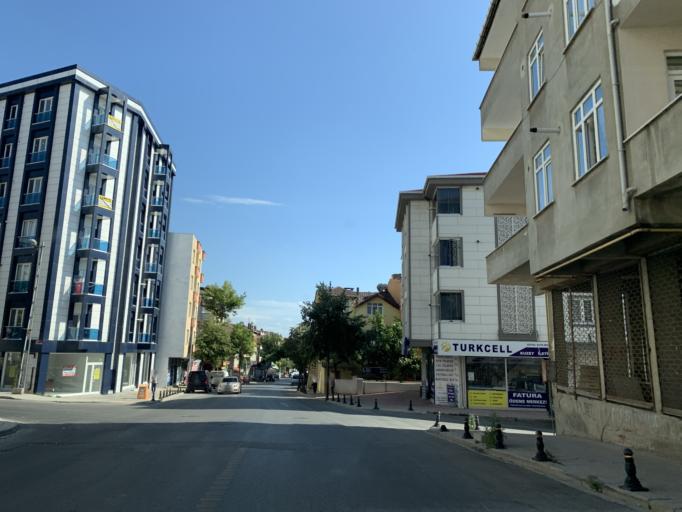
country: TR
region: Istanbul
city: Pendik
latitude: 40.8793
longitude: 29.2809
